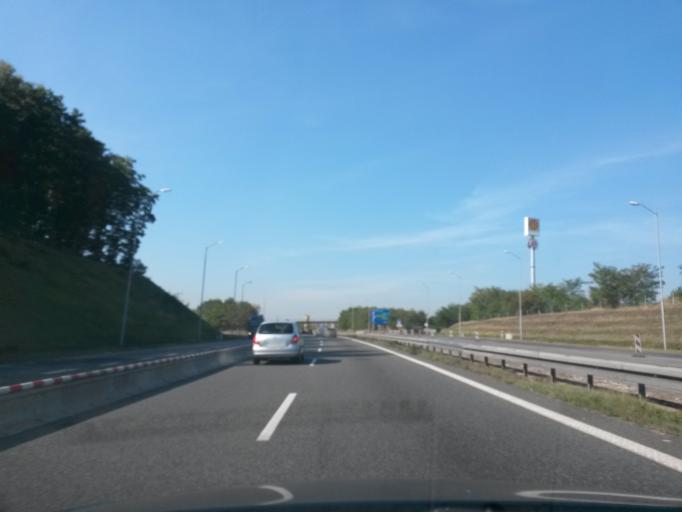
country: PL
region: Silesian Voivodeship
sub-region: Ruda Slaska
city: Ruda Slaska
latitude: 50.2503
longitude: 18.8859
